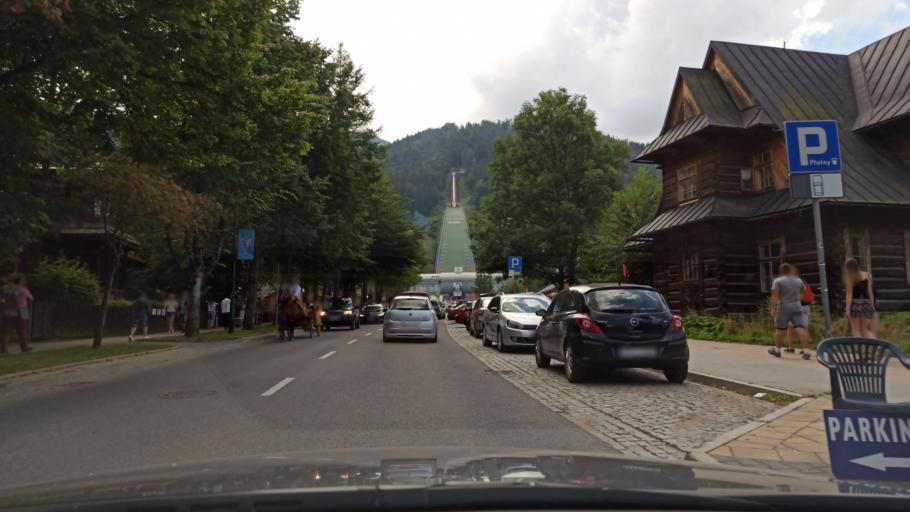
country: PL
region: Lesser Poland Voivodeship
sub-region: Powiat tatrzanski
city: Zakopane
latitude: 49.2830
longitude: 19.9647
